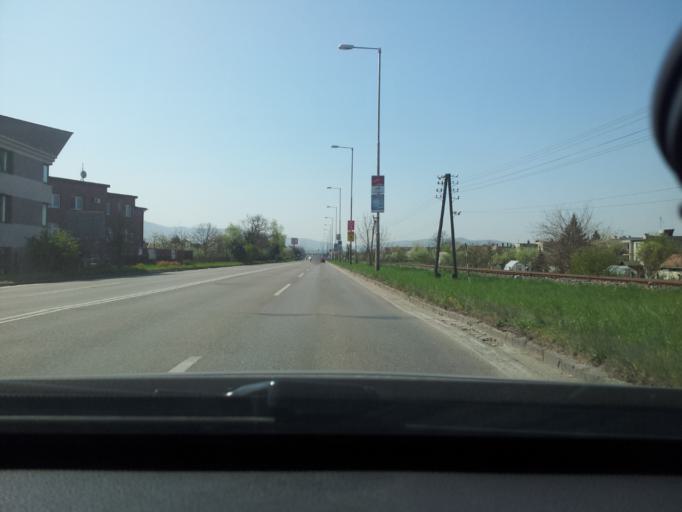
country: SK
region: Trenciansky
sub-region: Okres Trencin
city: Trencin
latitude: 48.8824
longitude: 18.0264
